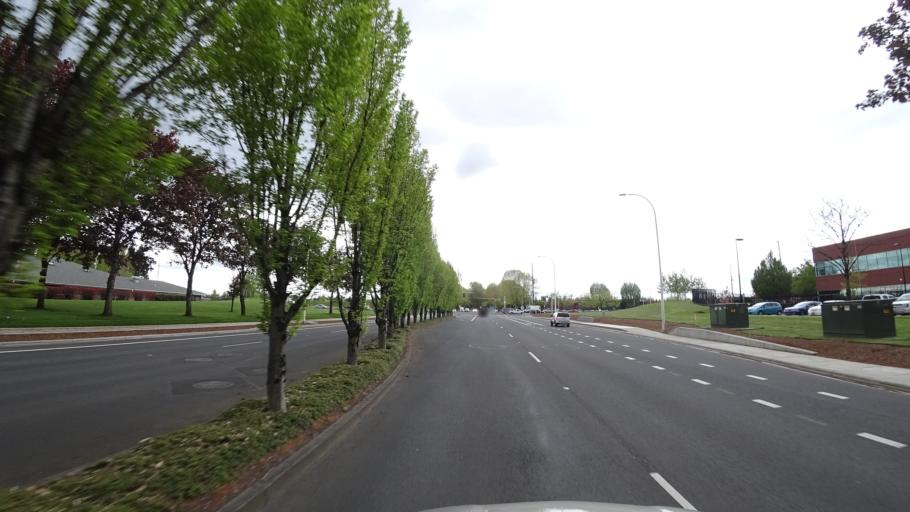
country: US
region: Oregon
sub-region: Washington County
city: Rockcreek
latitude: 45.5464
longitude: -122.8979
